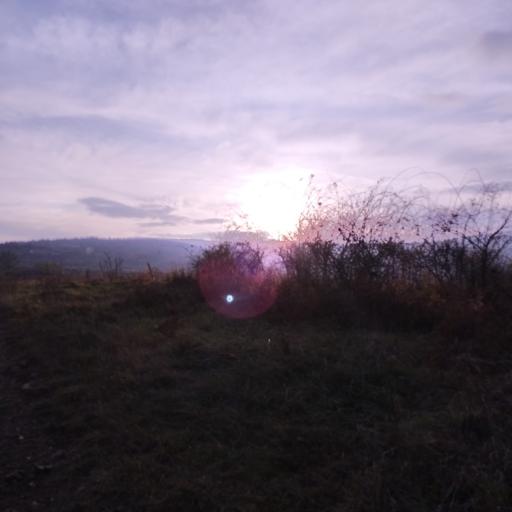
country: HU
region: Pest
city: Pomaz
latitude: 47.6270
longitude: 19.0218
